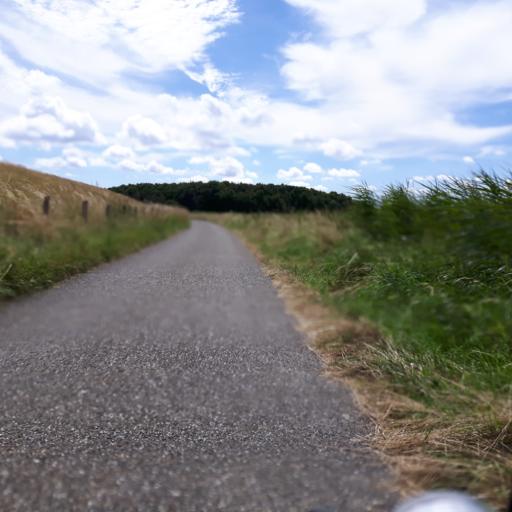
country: NL
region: Zeeland
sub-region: Gemeente Goes
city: Goes
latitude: 51.5627
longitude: 3.8950
